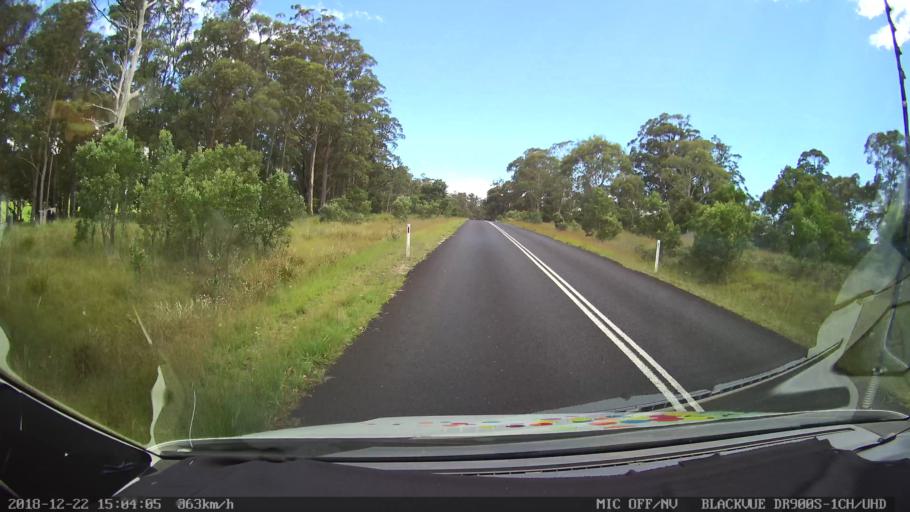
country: AU
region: New South Wales
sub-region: Bellingen
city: Dorrigo
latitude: -30.2712
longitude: 152.4384
